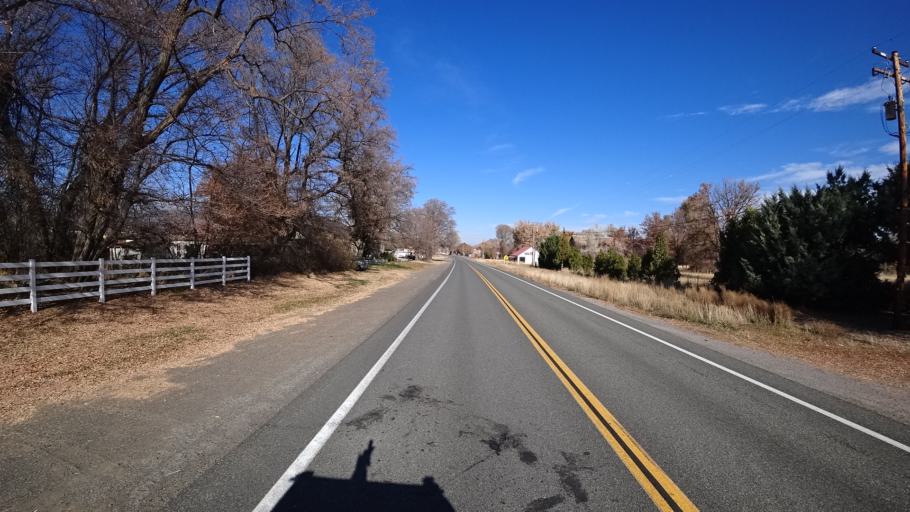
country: US
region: California
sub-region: Siskiyou County
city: Weed
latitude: 41.5181
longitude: -122.5192
